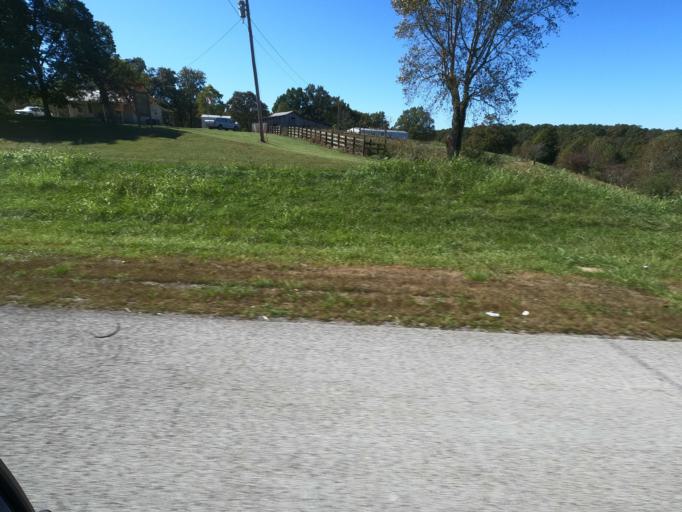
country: US
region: Tennessee
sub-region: Maury County
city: Mount Pleasant
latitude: 35.4553
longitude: -87.2679
